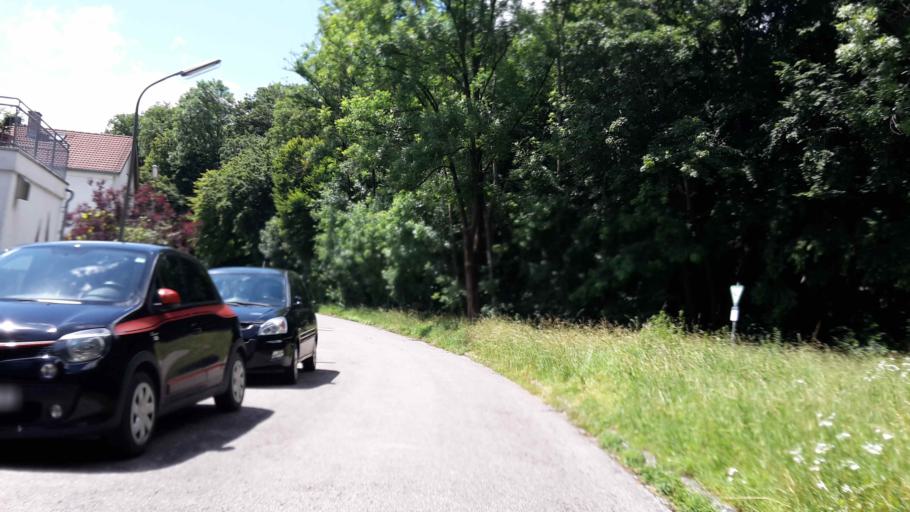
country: DE
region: Bavaria
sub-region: Upper Bavaria
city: Karlsfeld
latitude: 48.1872
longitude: 11.4779
